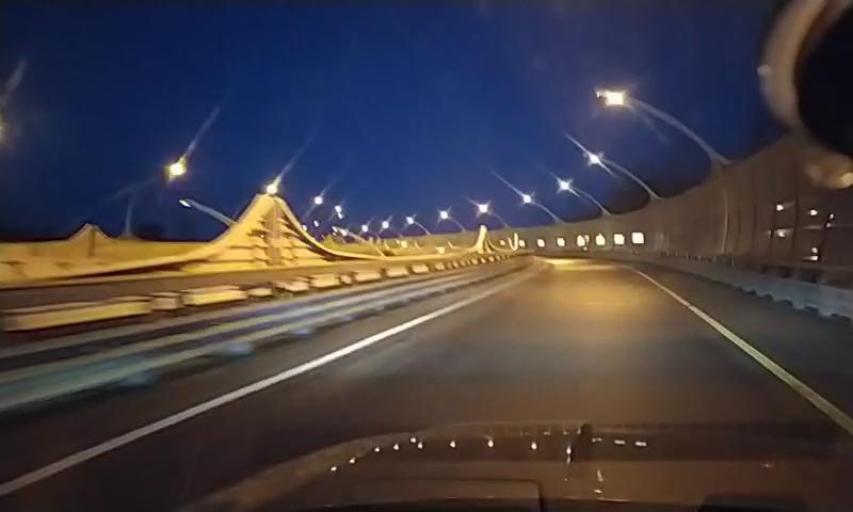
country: RU
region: St.-Petersburg
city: Beloostrov
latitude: 60.1498
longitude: 29.9904
